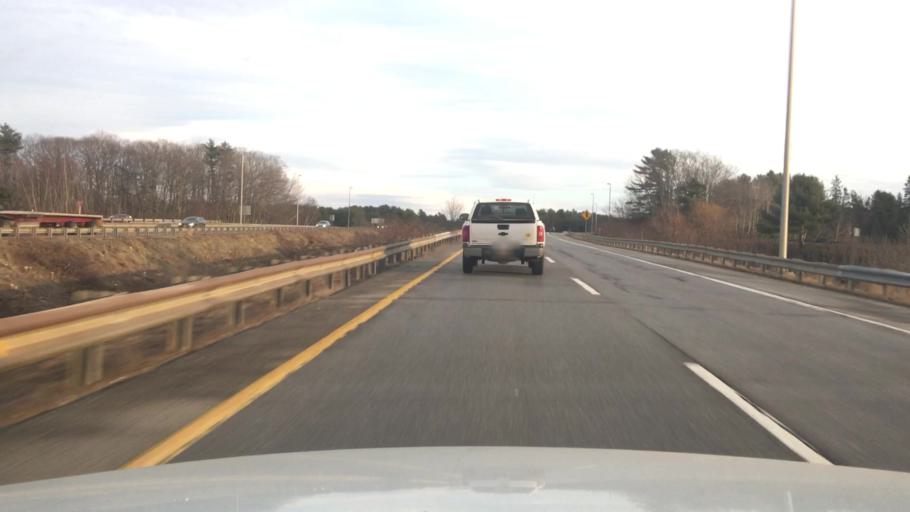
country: US
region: Maine
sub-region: Sagadahoc County
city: Bath
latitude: 43.9171
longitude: -69.8614
